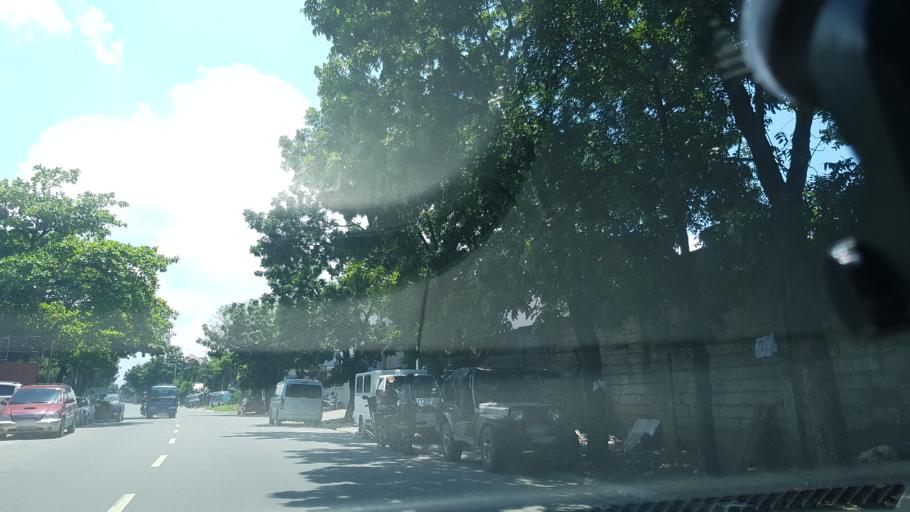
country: PH
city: Sambayanihan People's Village
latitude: 14.4685
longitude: 120.9969
